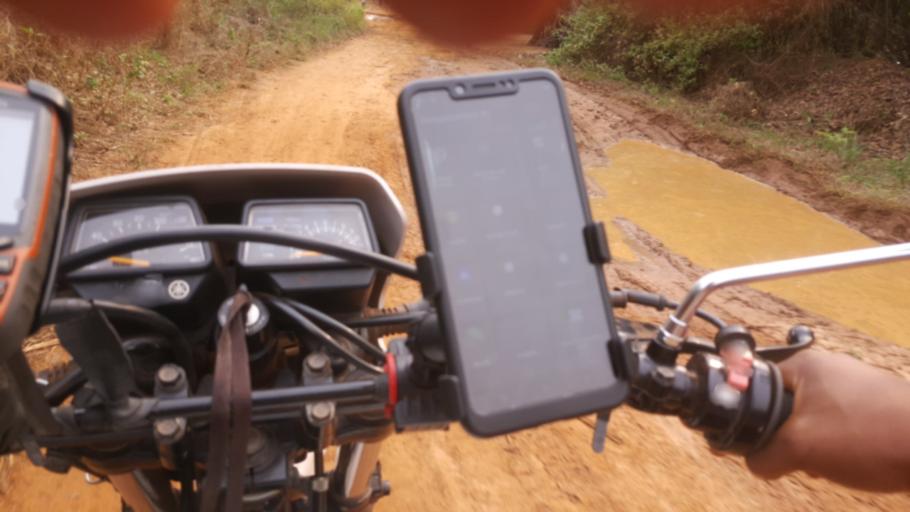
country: CD
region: Bandundu
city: Bandundu
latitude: -3.4647
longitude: 17.7159
